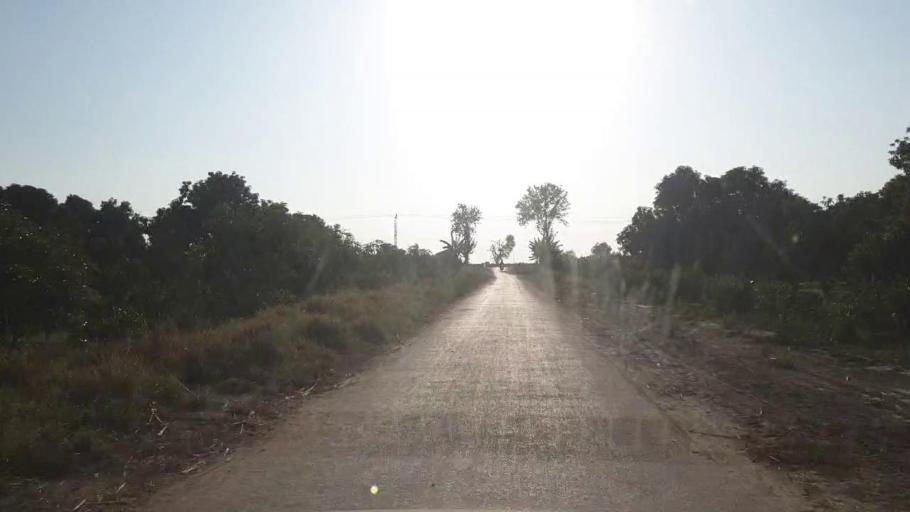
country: PK
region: Sindh
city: Tando Allahyar
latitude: 25.3630
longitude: 68.6819
